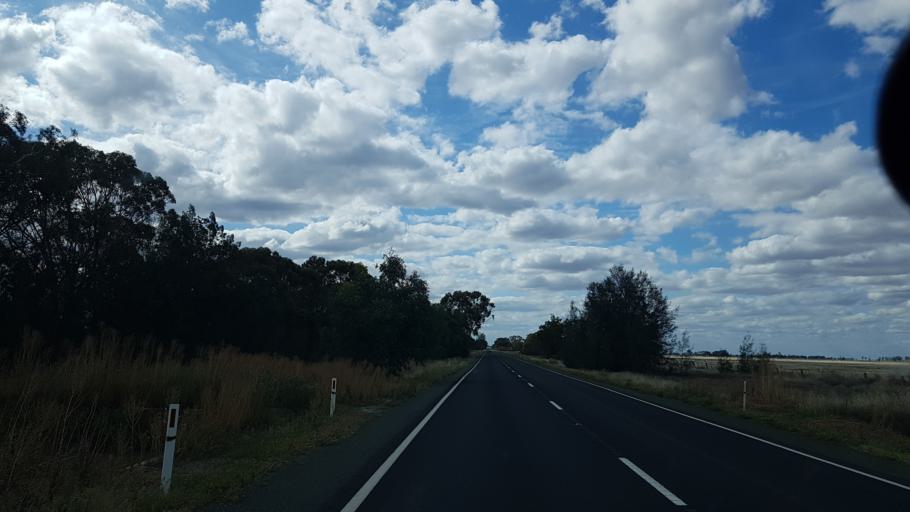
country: AU
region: Victoria
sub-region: Swan Hill
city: Swan Hill
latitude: -35.9871
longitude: 143.9458
